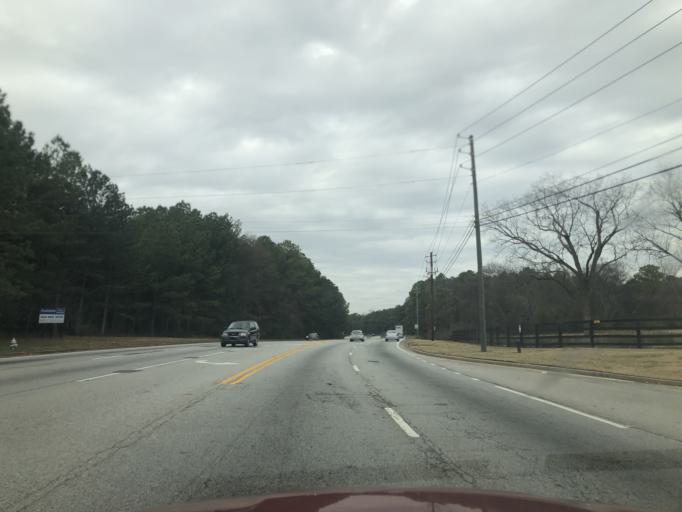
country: US
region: Georgia
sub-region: Clayton County
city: Conley
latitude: 33.6338
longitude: -84.2963
